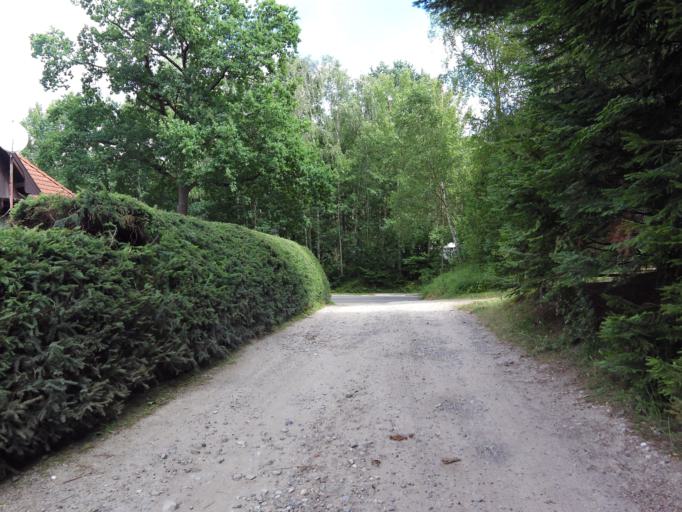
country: DE
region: Brandenburg
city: Lychen
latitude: 53.2225
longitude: 13.2798
